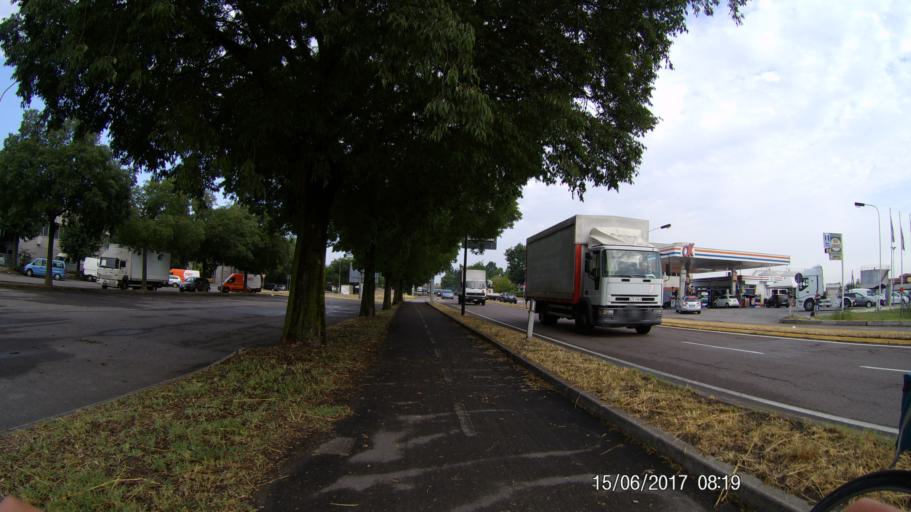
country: IT
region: Emilia-Romagna
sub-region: Provincia di Reggio Emilia
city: Roncocesi
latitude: 44.7172
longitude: 10.5773
